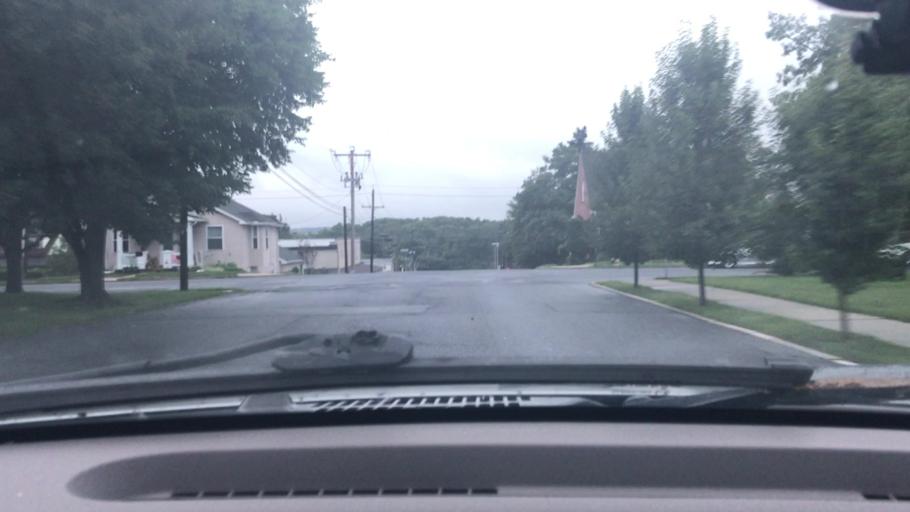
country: US
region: Pennsylvania
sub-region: Dauphin County
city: Palmdale
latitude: 40.2980
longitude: -76.6216
